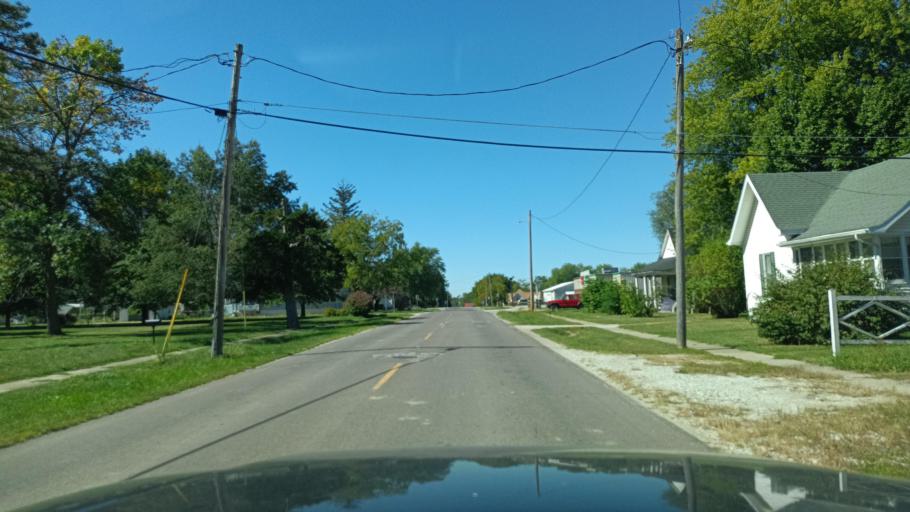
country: US
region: Missouri
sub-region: Macon County
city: La Plata
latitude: 40.0210
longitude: -92.4891
